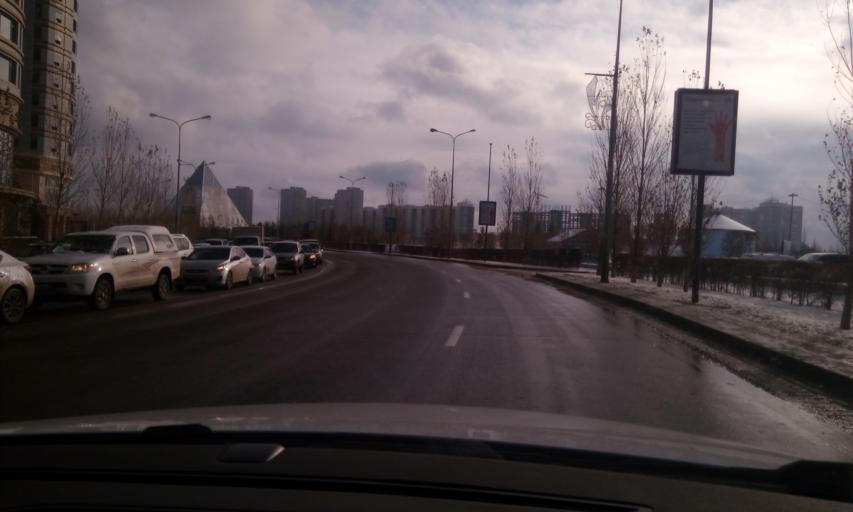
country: KZ
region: Astana Qalasy
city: Astana
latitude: 51.1287
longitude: 71.4579
